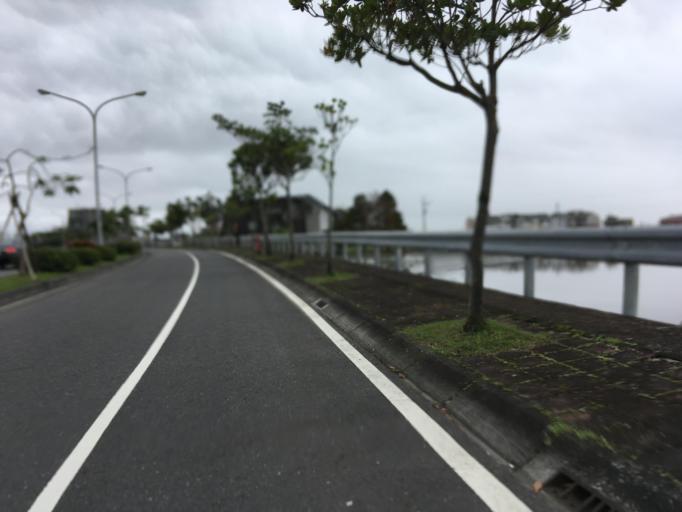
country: TW
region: Taiwan
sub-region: Yilan
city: Yilan
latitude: 24.7232
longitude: 121.7708
